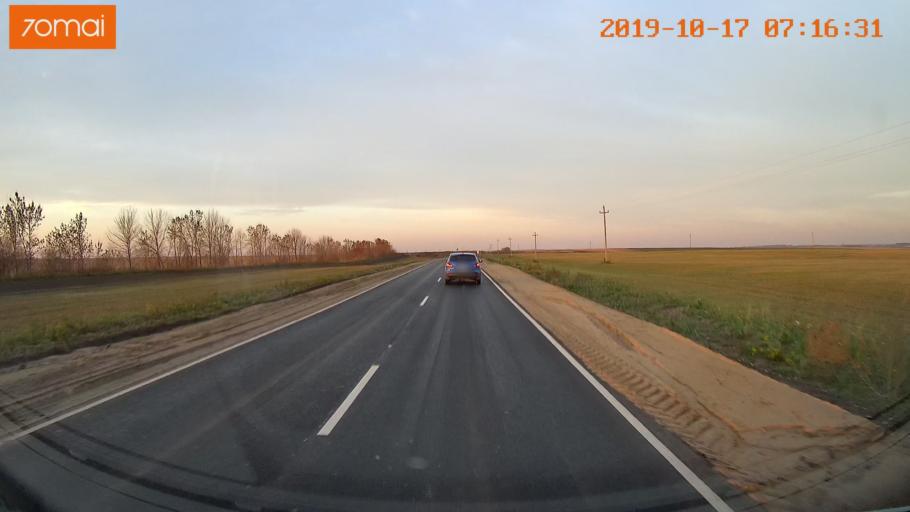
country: RU
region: Vladimir
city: Suzdal'
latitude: 56.3717
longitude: 40.2473
